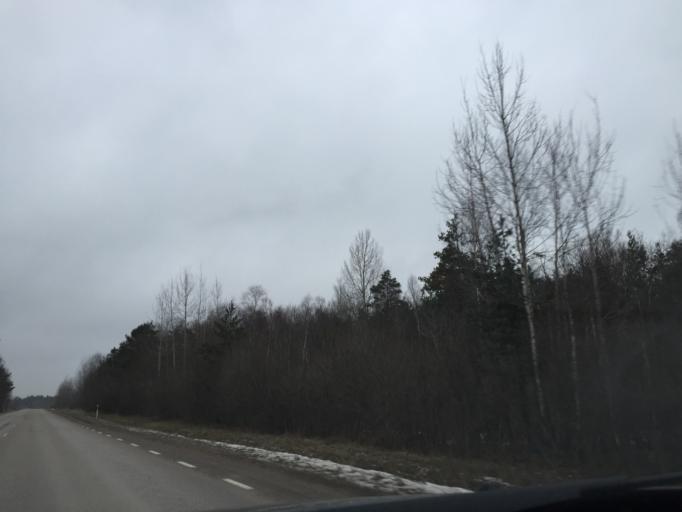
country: EE
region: Saare
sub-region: Kuressaare linn
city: Kuressaare
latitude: 58.2811
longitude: 22.4296
